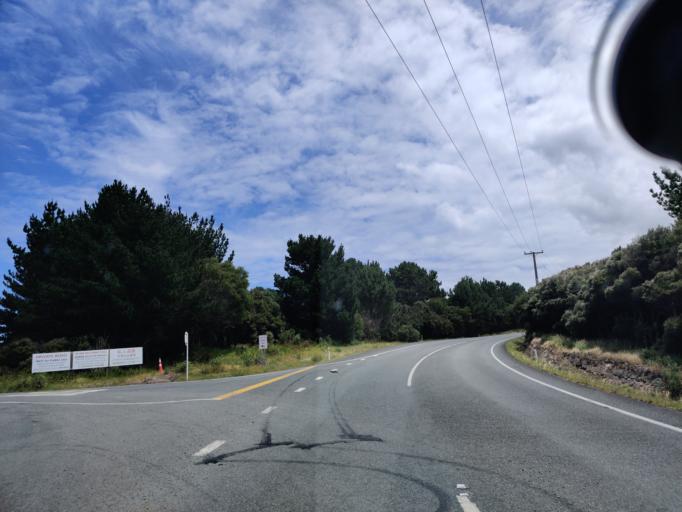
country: NZ
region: Northland
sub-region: Far North District
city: Kaitaia
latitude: -34.6634
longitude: 172.9694
